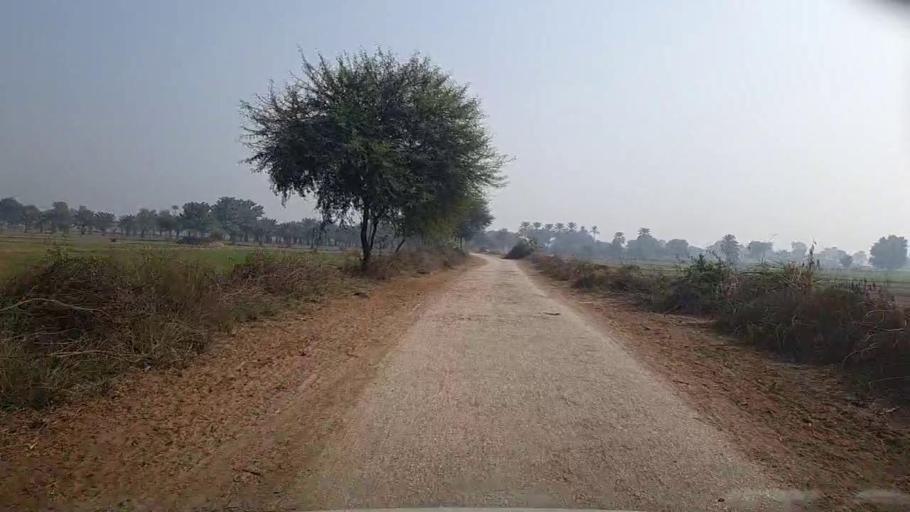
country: PK
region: Sindh
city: Setharja Old
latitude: 27.1429
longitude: 68.4925
